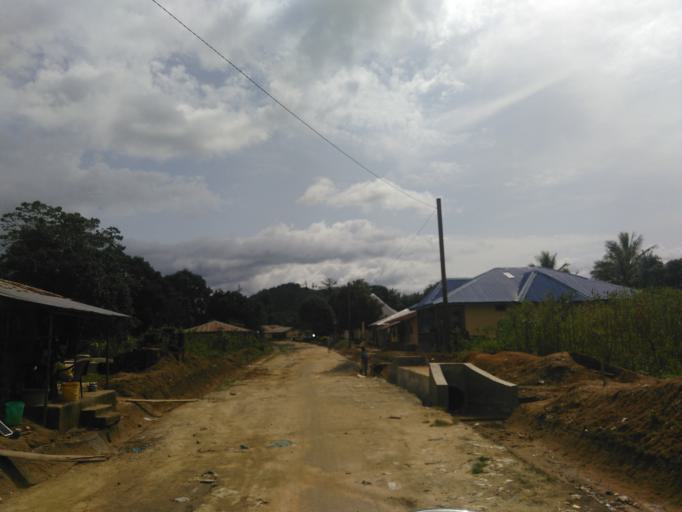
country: SL
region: Northern Province
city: Makali
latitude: 8.6288
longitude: -11.6621
